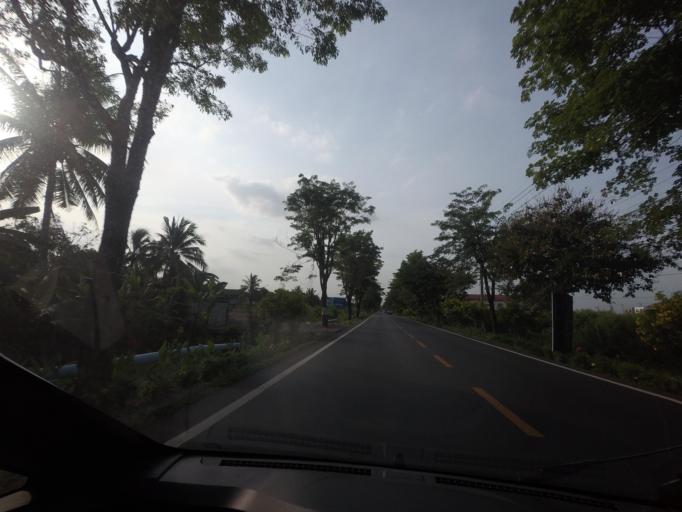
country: TH
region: Bangkok
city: Nong Chok
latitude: 13.8427
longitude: 100.8692
